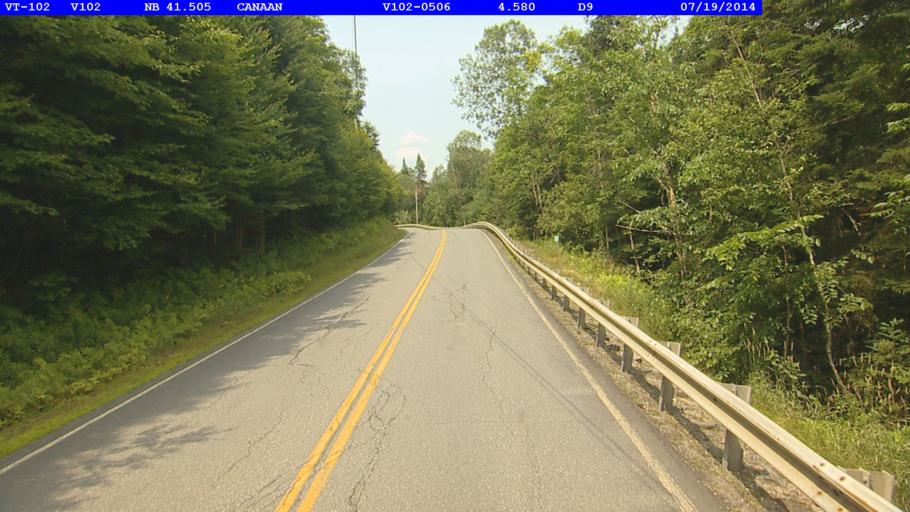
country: US
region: New Hampshire
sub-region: Coos County
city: Colebrook
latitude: 44.9703
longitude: -71.5268
